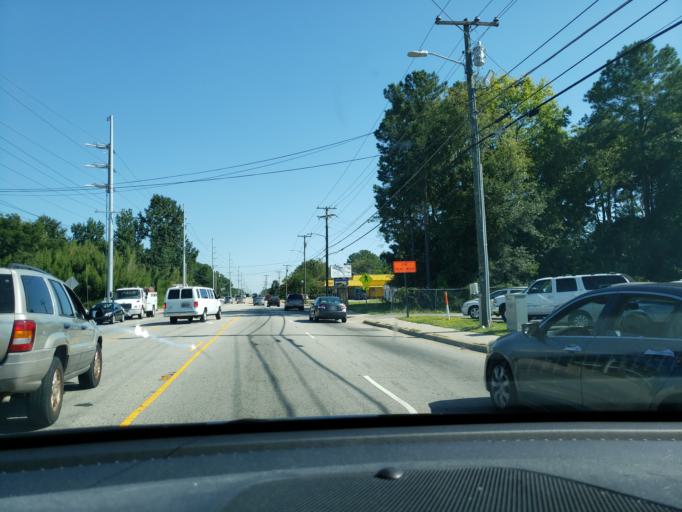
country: US
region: North Carolina
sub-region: Cumberland County
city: Fayetteville
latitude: 35.0959
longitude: -78.9147
